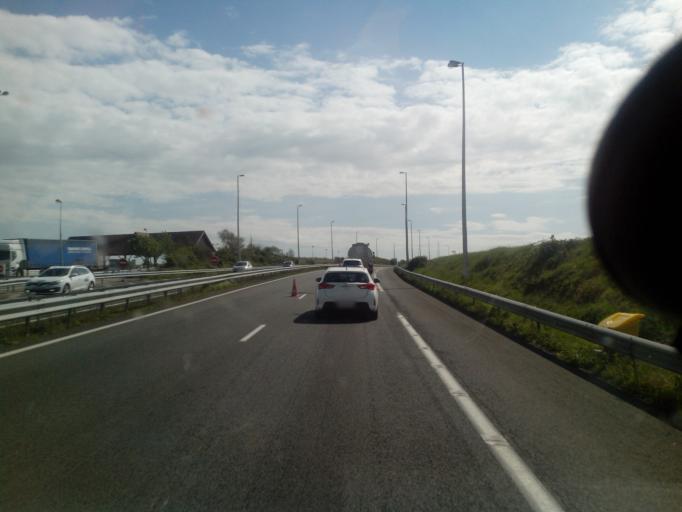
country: FR
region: Nord-Pas-de-Calais
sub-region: Departement du Pas-de-Calais
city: Marquise
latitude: 50.7940
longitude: 1.6874
